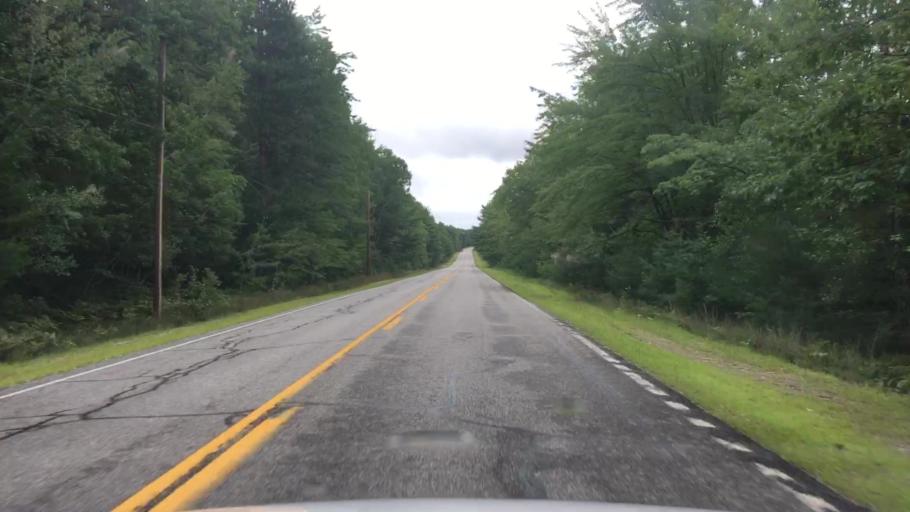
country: US
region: Maine
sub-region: Oxford County
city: Brownfield
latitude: 43.9295
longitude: -70.8799
